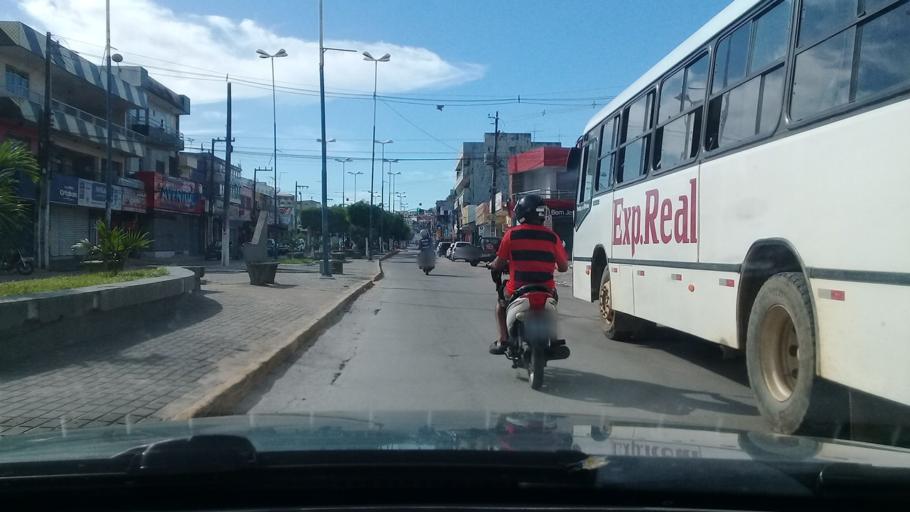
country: BR
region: Pernambuco
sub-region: Vitoria De Santo Antao
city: Vitoria de Santo Antao
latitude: -8.1213
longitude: -35.2951
